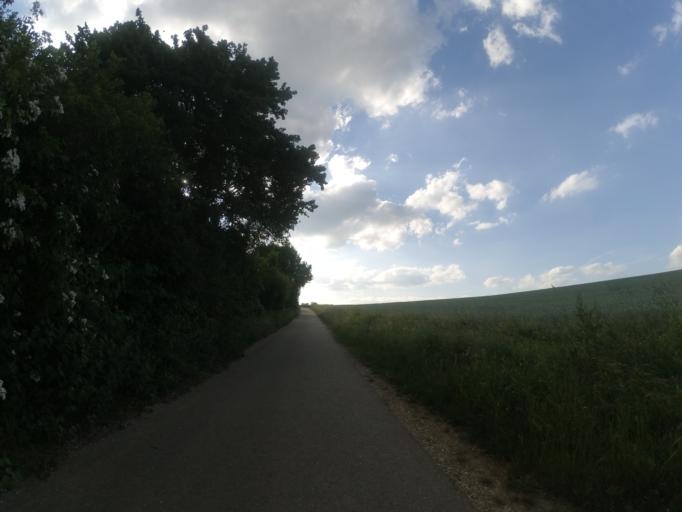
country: DE
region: Baden-Wuerttemberg
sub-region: Tuebingen Region
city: Ulm
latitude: 48.4342
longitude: 10.0005
